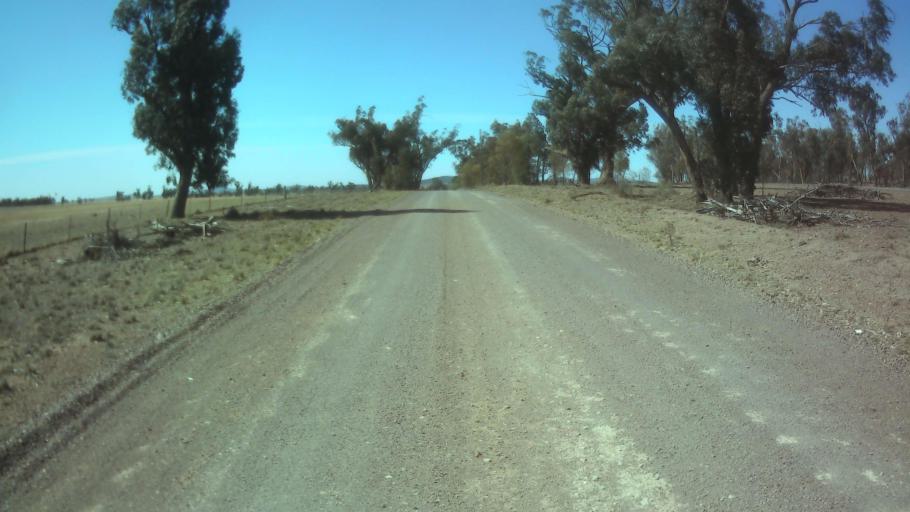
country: AU
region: New South Wales
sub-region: Forbes
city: Forbes
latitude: -33.7139
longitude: 147.7472
